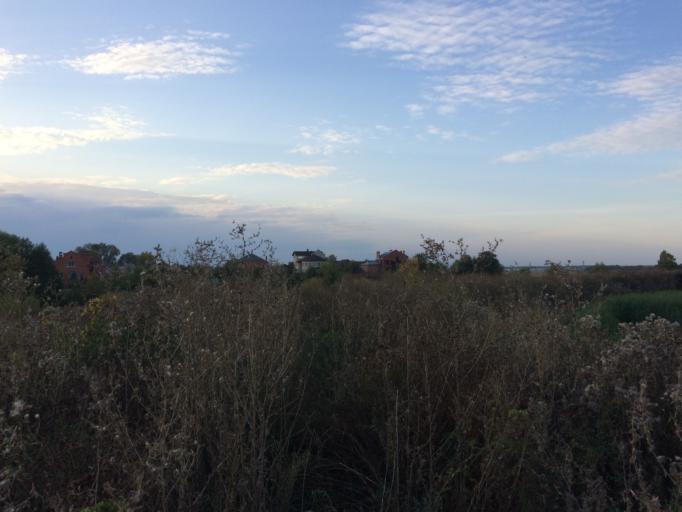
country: RU
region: Mariy-El
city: Yoshkar-Ola
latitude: 56.6486
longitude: 47.9214
